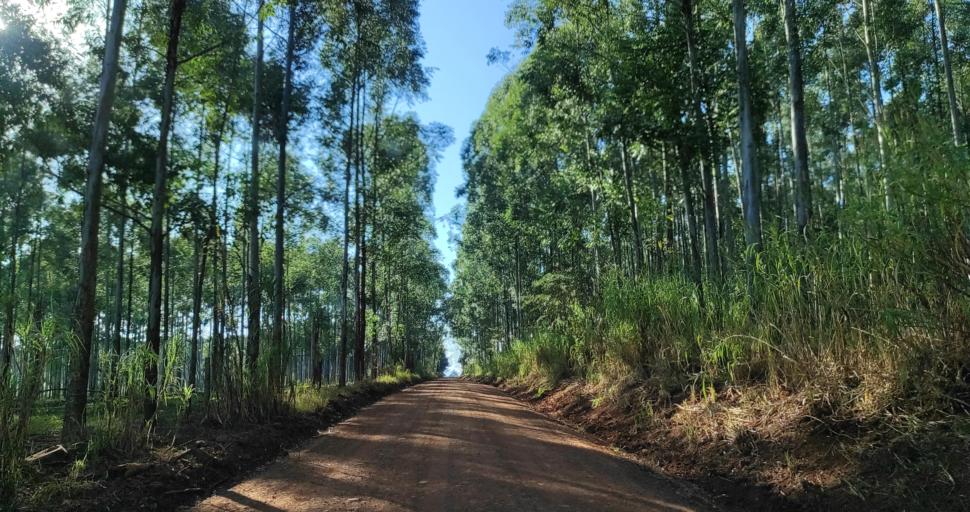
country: AR
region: Misiones
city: Capiovi
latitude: -26.8801
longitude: -55.0452
